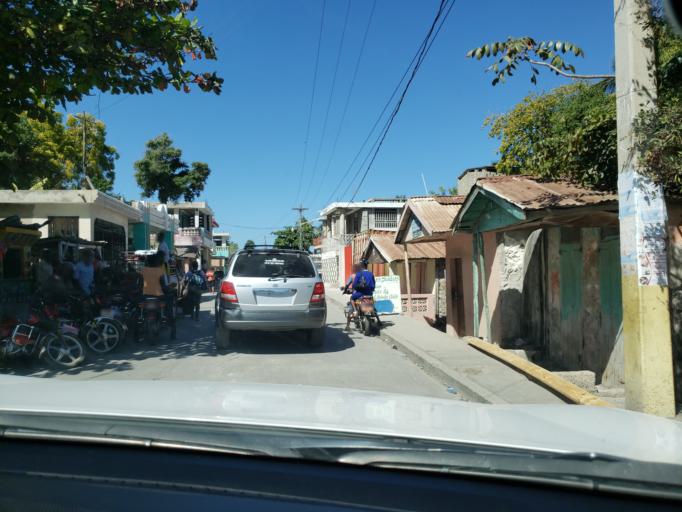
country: HT
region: Nippes
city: Miragoane
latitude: 18.4429
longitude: -73.0924
